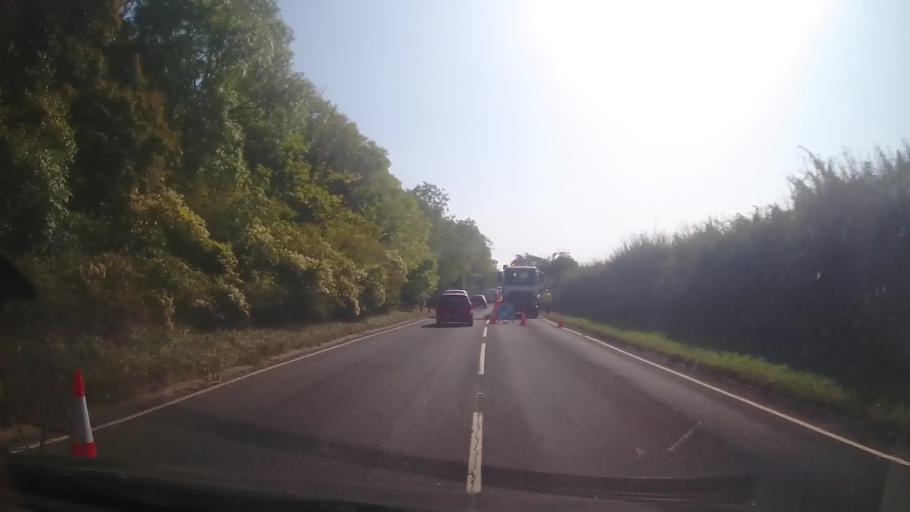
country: GB
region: England
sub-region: Worcestershire
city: Evesham
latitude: 52.1232
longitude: -1.9813
